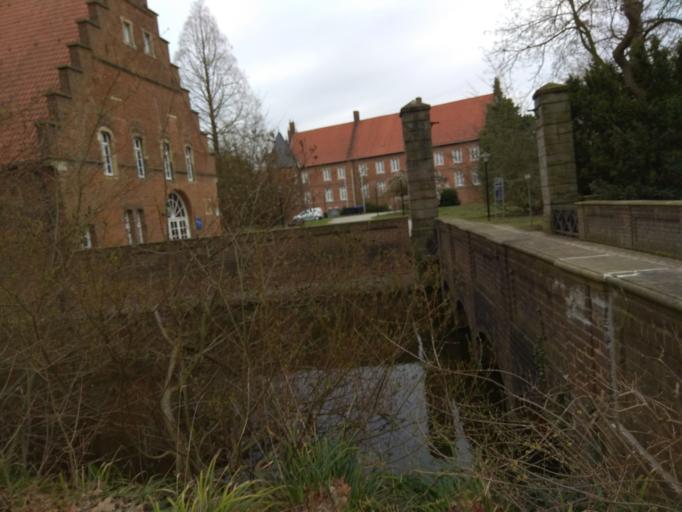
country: DE
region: North Rhine-Westphalia
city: Herten
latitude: 51.5913
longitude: 7.1287
